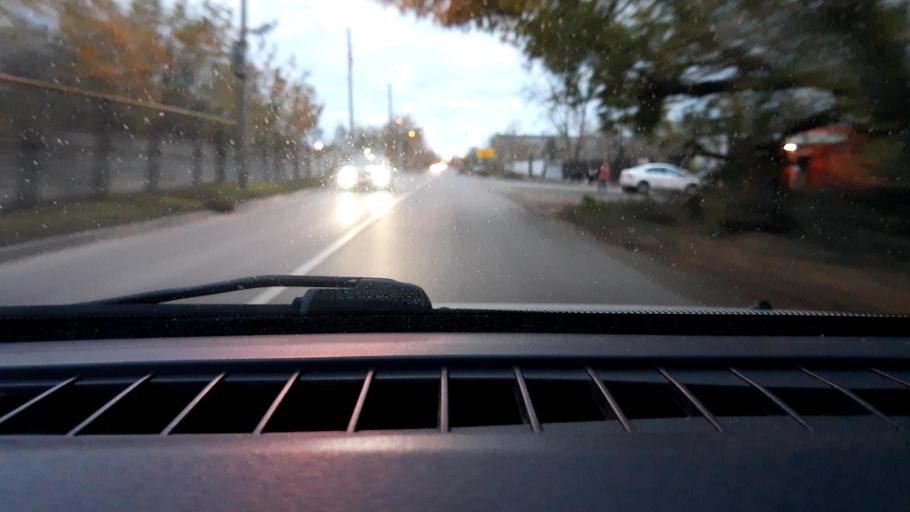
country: RU
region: Nizjnij Novgorod
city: Gorbatovka
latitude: 56.3470
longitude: 43.8207
